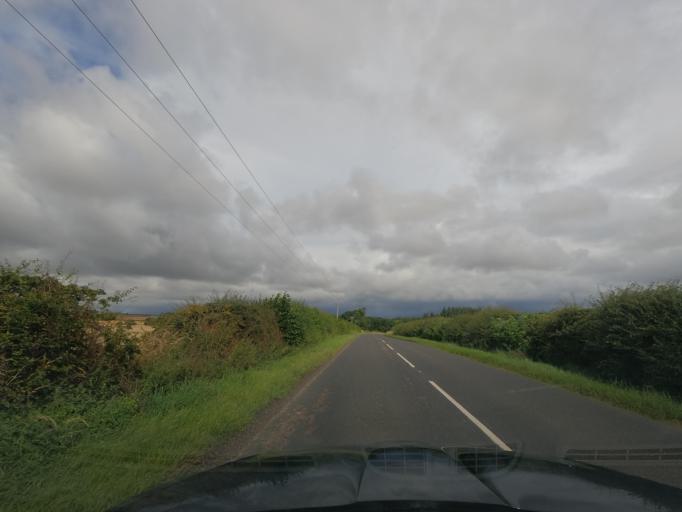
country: GB
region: England
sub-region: Northumberland
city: Ancroft
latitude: 55.6795
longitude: -2.0025
